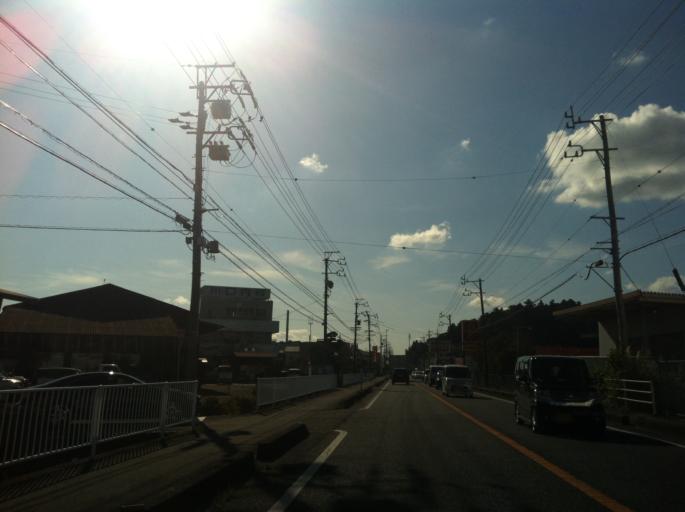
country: JP
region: Shizuoka
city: Fujieda
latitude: 34.8880
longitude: 138.2780
